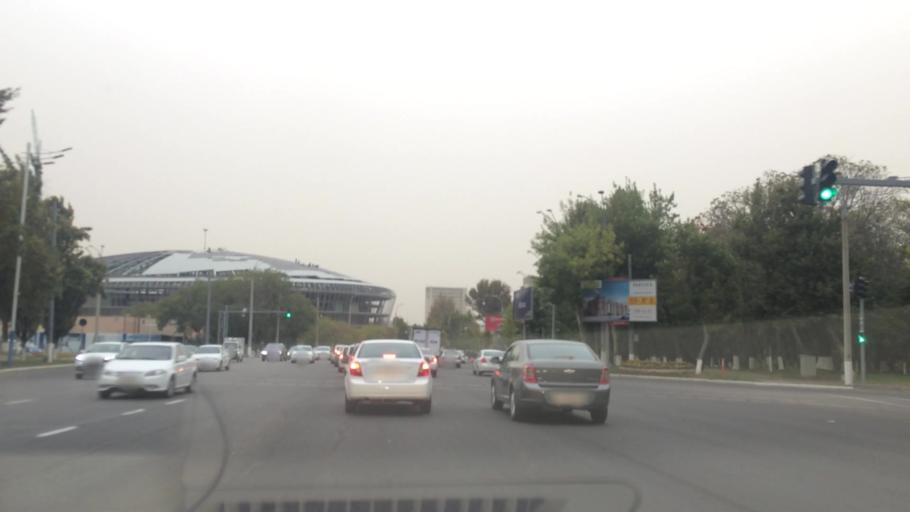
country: UZ
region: Toshkent Shahri
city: Tashkent
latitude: 41.3077
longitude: 69.2563
